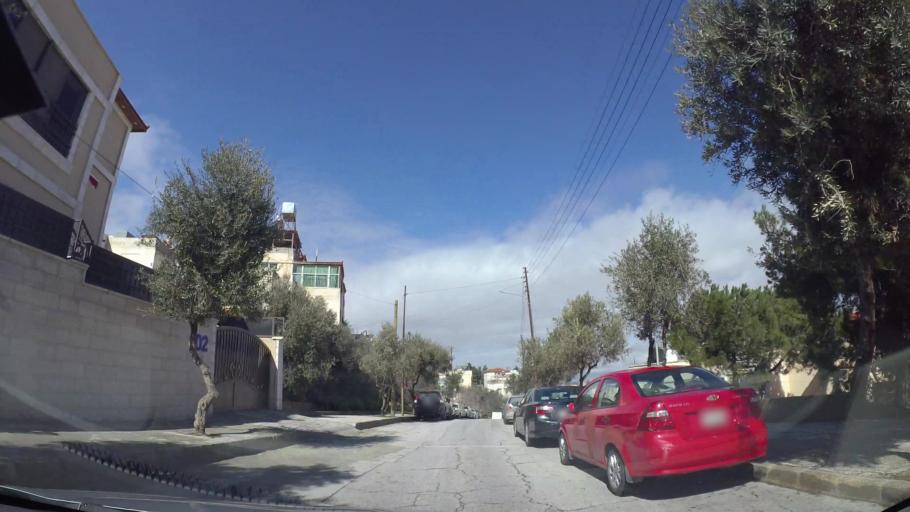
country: JO
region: Amman
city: Al Jubayhah
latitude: 32.0562
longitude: 35.8816
